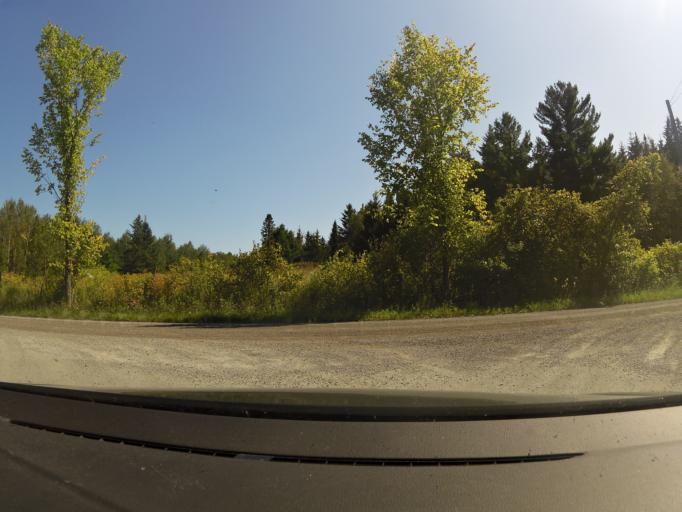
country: CA
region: Ontario
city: Bells Corners
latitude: 45.2926
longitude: -75.9850
